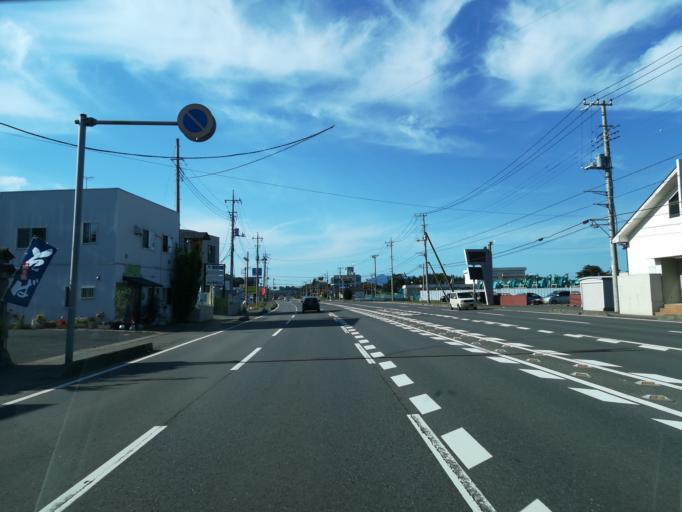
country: JP
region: Ibaraki
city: Naka
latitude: 36.0504
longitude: 140.0852
